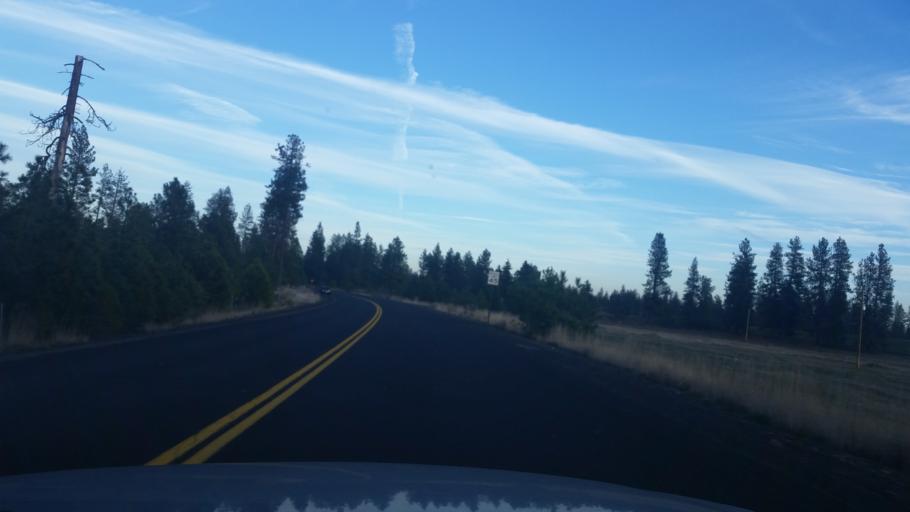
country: US
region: Washington
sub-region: Spokane County
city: Cheney
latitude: 47.4800
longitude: -117.5191
